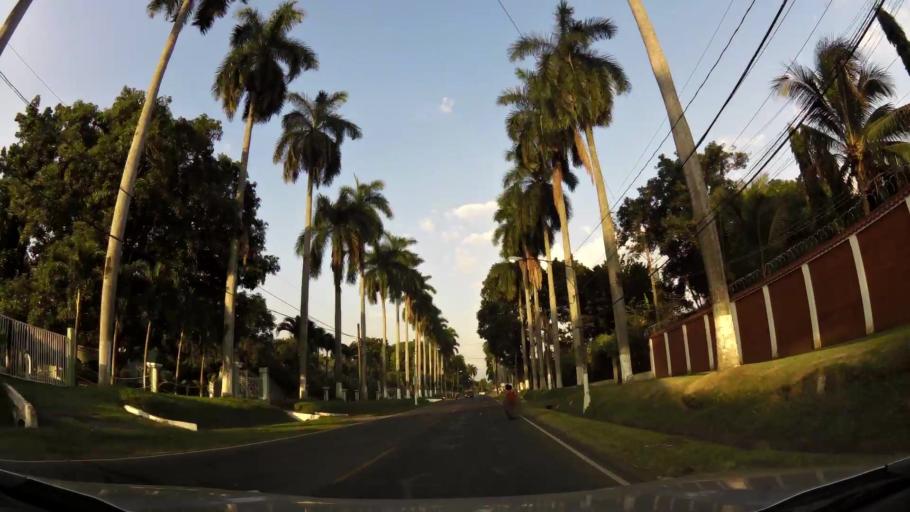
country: GT
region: Retalhuleu
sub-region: Municipio de Retalhuleu
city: Retalhuleu
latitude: 14.5450
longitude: -91.6674
